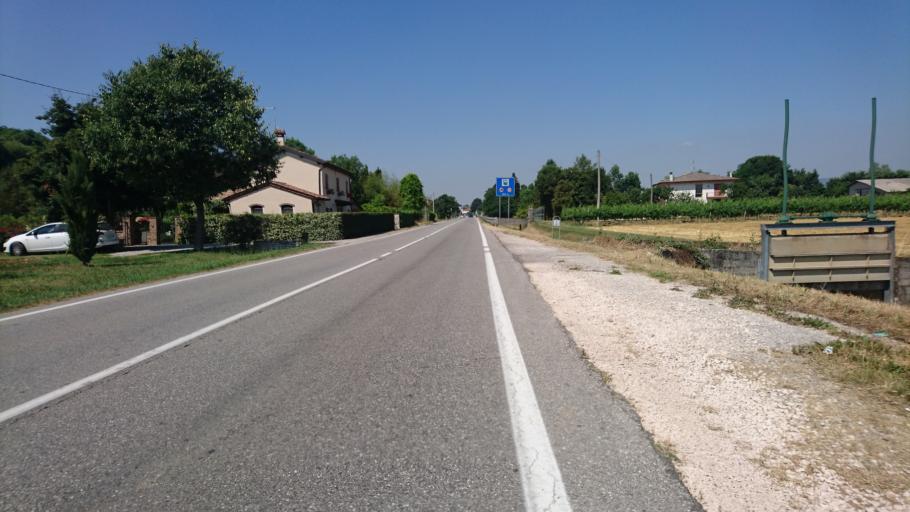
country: IT
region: Veneto
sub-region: Provincia di Padova
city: Bastia
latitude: 45.3940
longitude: 11.6709
